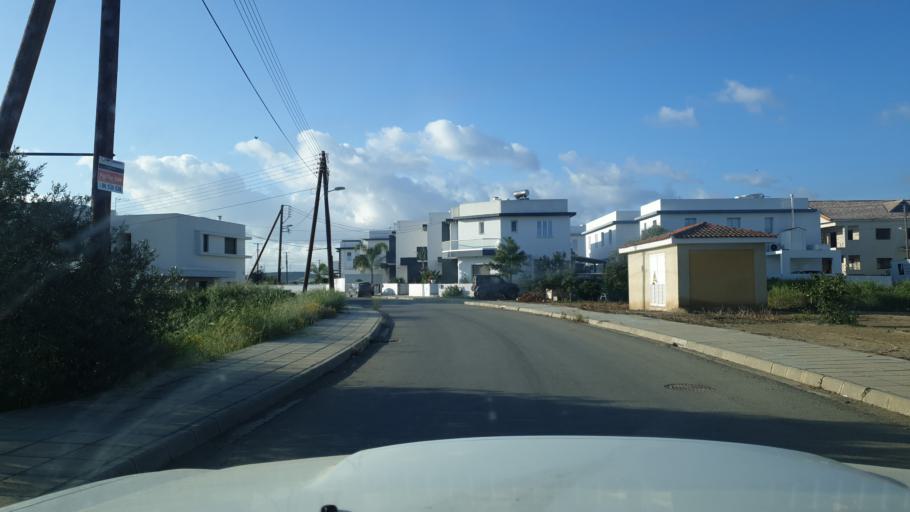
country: CY
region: Lefkosia
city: Tseri
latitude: 35.0649
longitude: 33.3272
